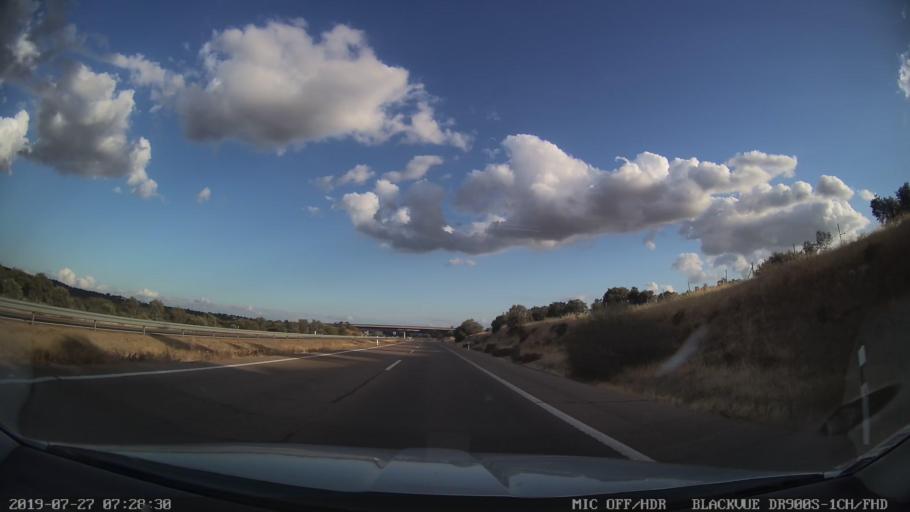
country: ES
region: Extremadura
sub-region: Provincia de Caceres
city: Villamesias
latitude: 39.2246
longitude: -5.8839
